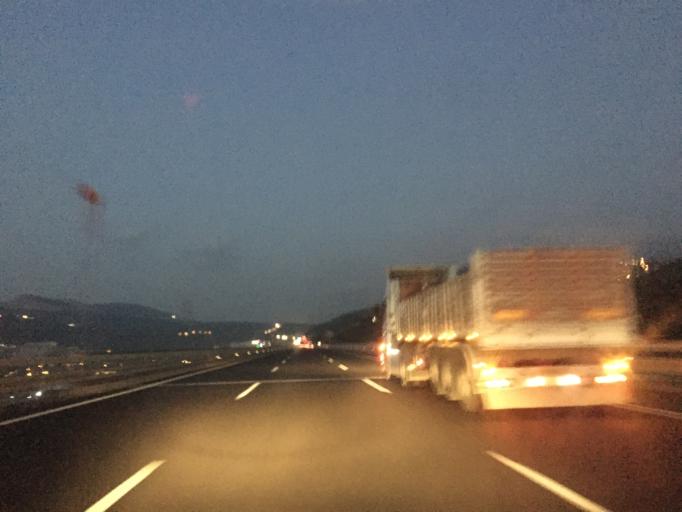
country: TR
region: Bursa
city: Gemlik
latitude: 40.4190
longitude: 29.1608
